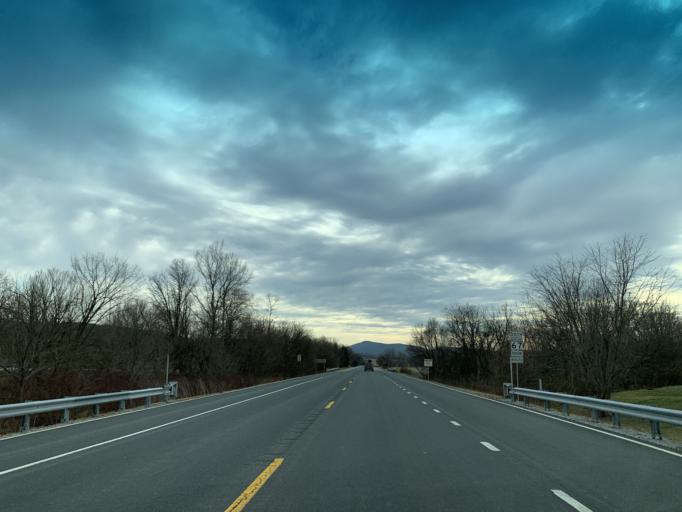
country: US
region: Maryland
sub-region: Washington County
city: Boonsboro
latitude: 39.4728
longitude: -77.6554
